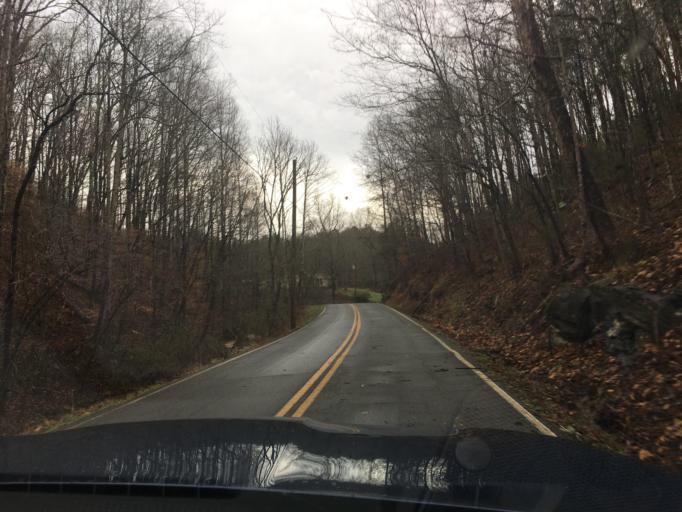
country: US
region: Tennessee
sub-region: McMinn County
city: Englewood
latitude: 35.3712
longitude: -84.4357
